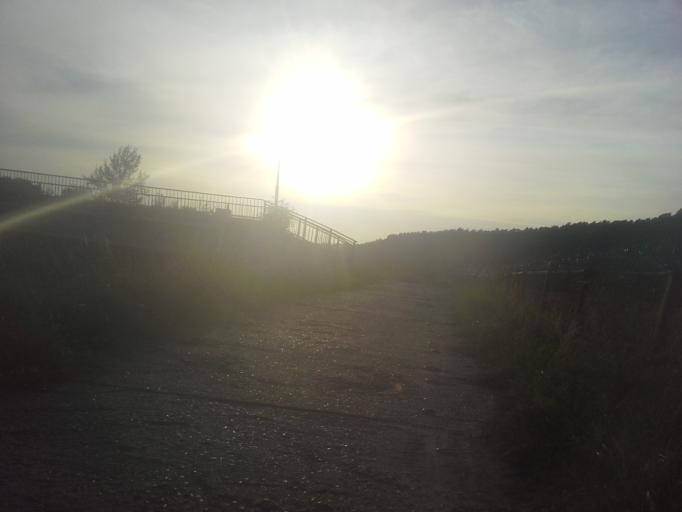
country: RU
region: Moskovskaya
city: Nikolina Gora
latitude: 55.7279
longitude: 37.0894
